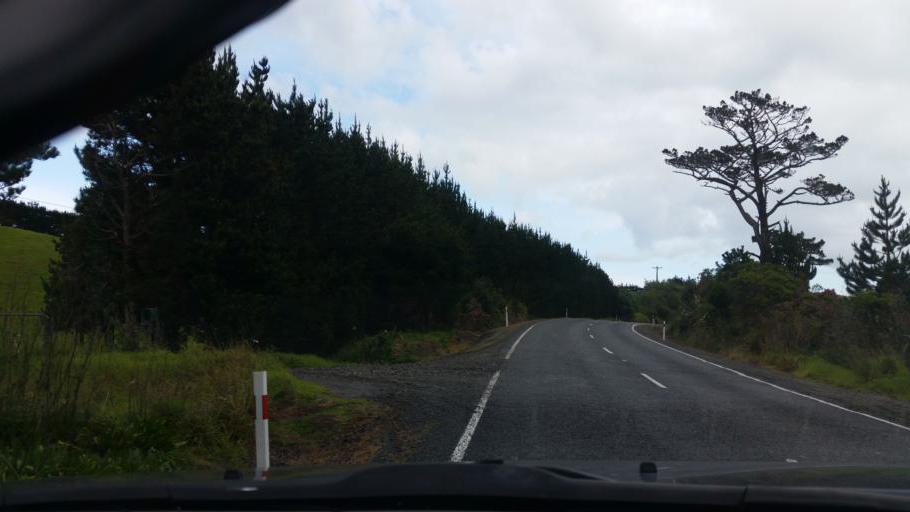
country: NZ
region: Northland
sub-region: Kaipara District
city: Dargaville
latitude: -35.9478
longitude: 173.7695
